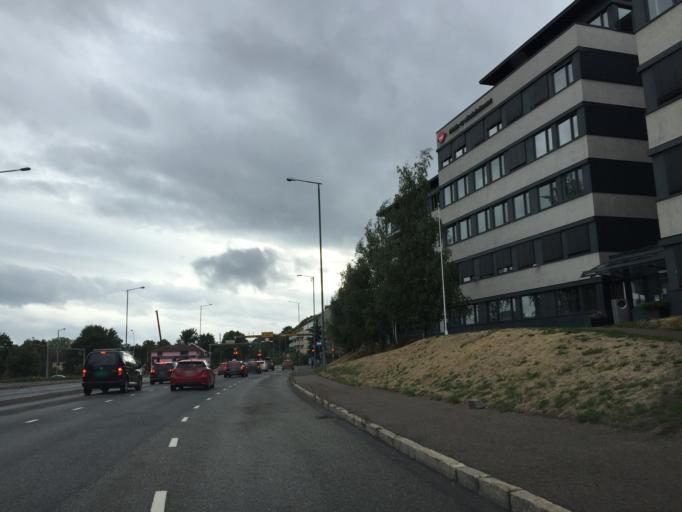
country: NO
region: Oslo
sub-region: Oslo
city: Oslo
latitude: 59.9247
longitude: 10.7933
